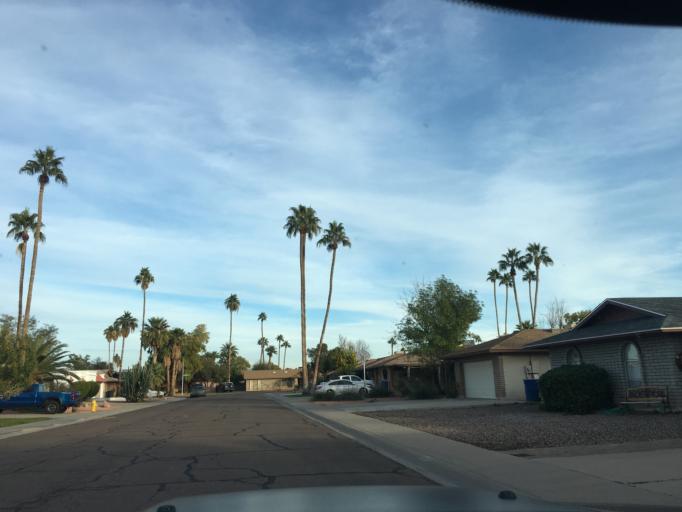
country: US
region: Arizona
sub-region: Maricopa County
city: Tempe
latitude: 33.3740
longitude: -111.9069
